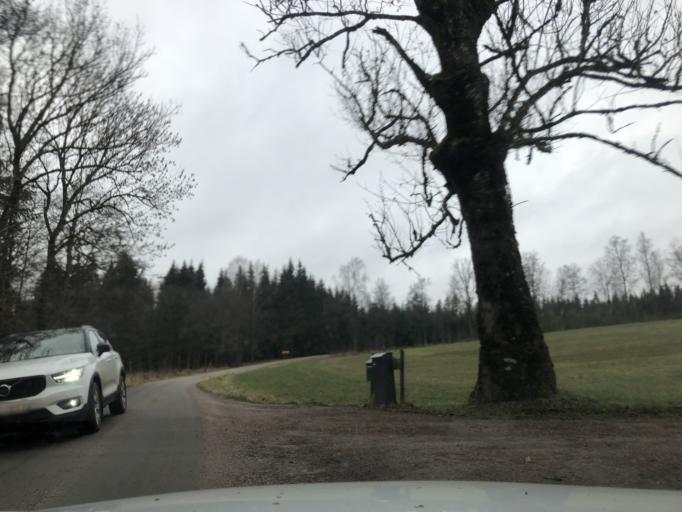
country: SE
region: Vaestra Goetaland
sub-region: Ulricehamns Kommun
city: Ulricehamn
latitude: 57.8577
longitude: 13.6203
